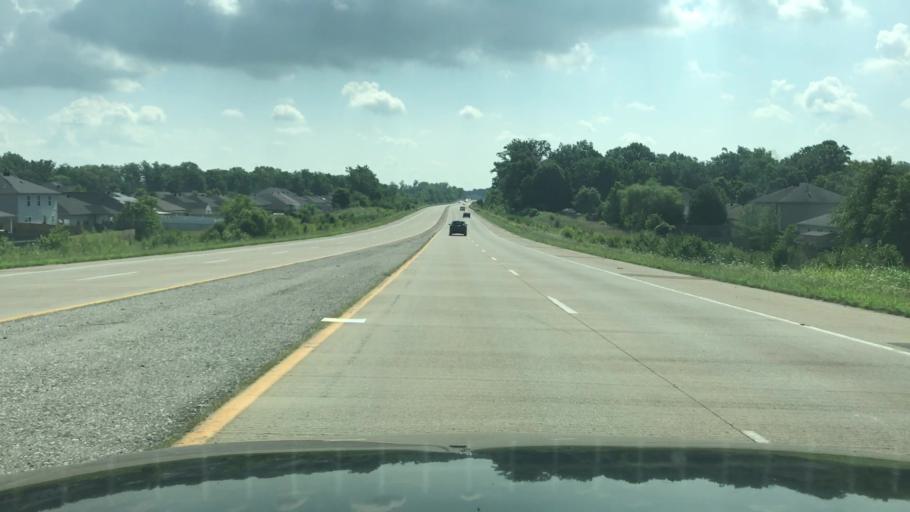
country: US
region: Indiana
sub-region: Vanderburgh County
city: Melody Hill
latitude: 38.0131
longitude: -87.5074
